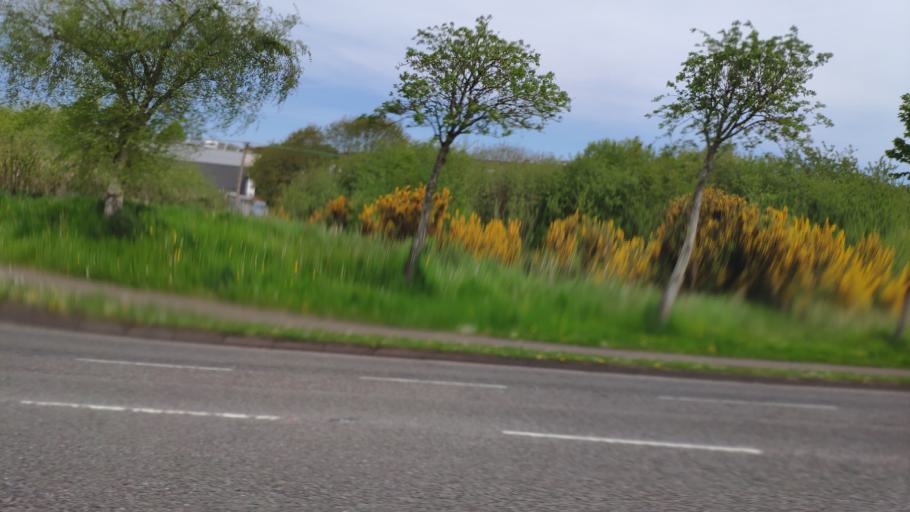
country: IE
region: Munster
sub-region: County Cork
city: Cork
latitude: 51.9150
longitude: -8.4487
